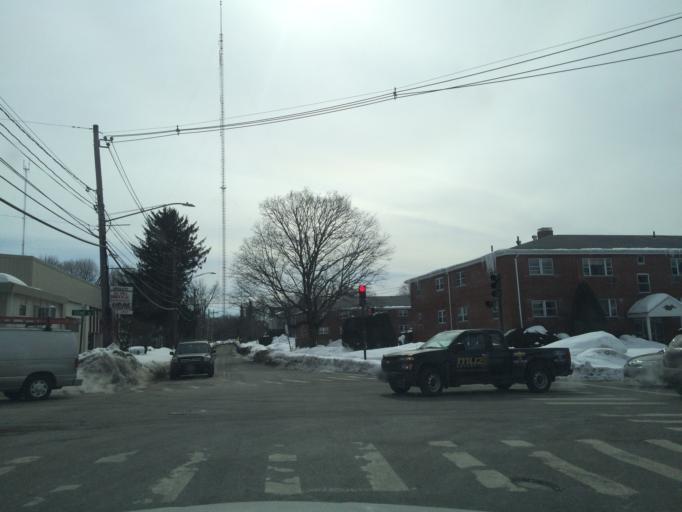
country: US
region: Massachusetts
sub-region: Middlesex County
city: Newton
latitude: 42.3130
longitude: -71.2247
